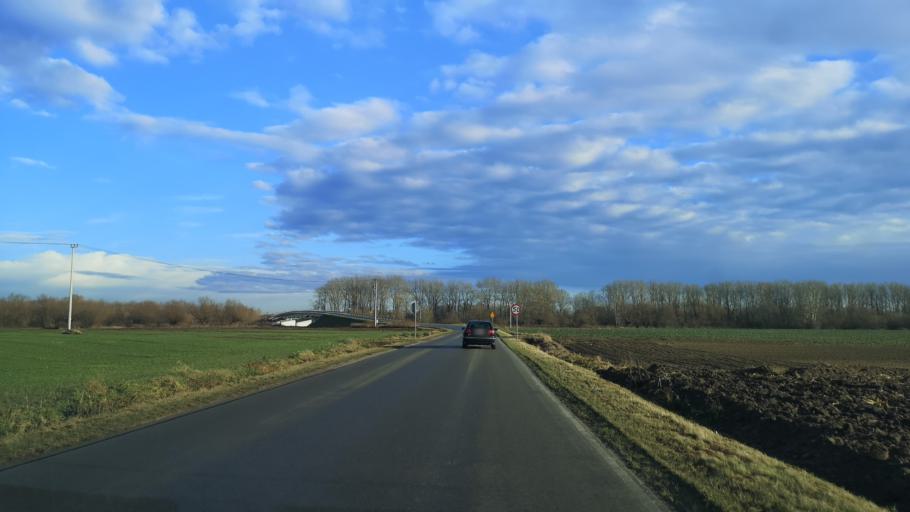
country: PL
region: Subcarpathian Voivodeship
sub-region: Powiat lezajski
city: Piskorowice
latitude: 50.2465
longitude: 22.4960
